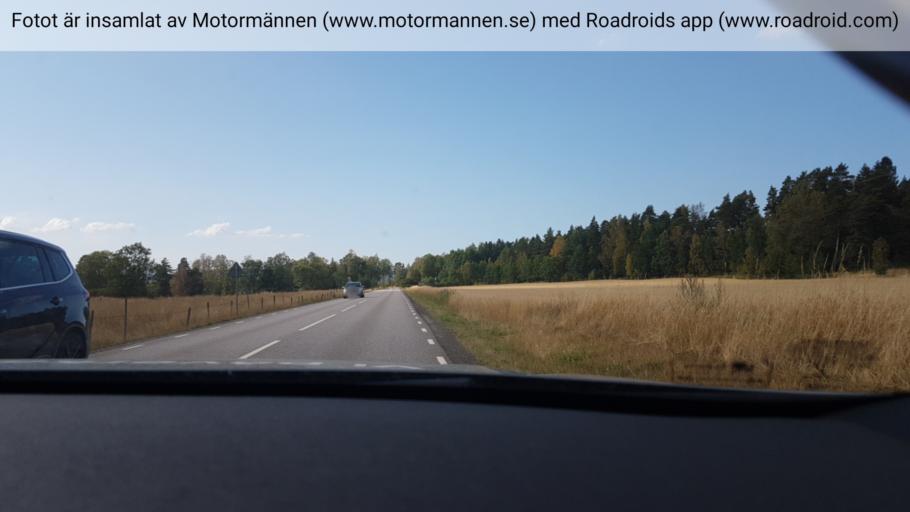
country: SE
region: Vaestra Goetaland
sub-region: Gotene Kommun
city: Goetene
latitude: 58.5601
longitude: 13.5045
